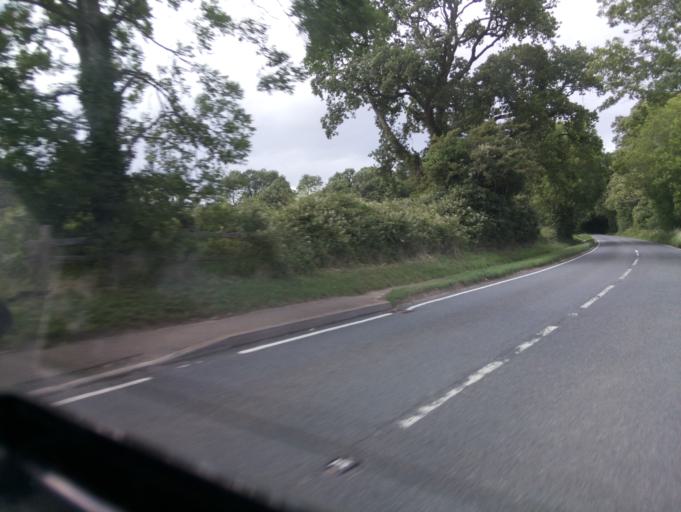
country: GB
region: England
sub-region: Gloucestershire
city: Chipping Campden
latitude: 52.0193
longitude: -1.7509
